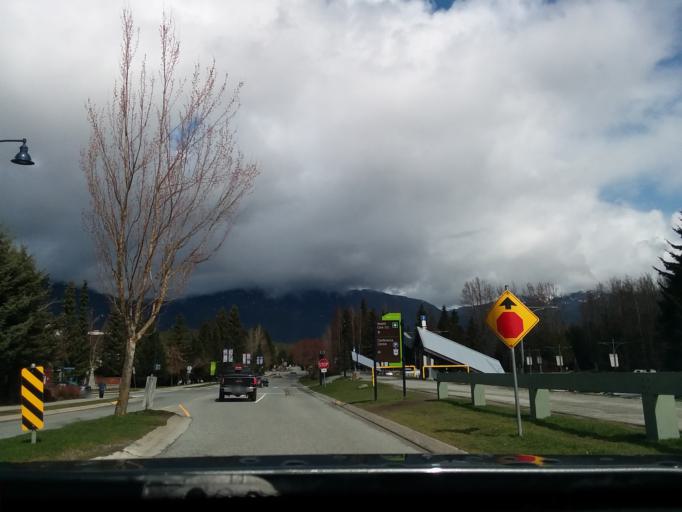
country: CA
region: British Columbia
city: Whistler
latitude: 50.1156
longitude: -122.9533
